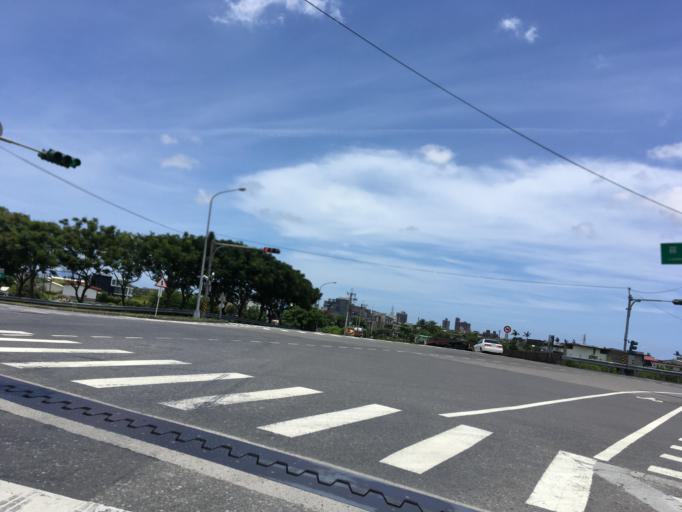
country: TW
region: Taiwan
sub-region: Yilan
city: Yilan
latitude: 24.7031
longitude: 121.7552
